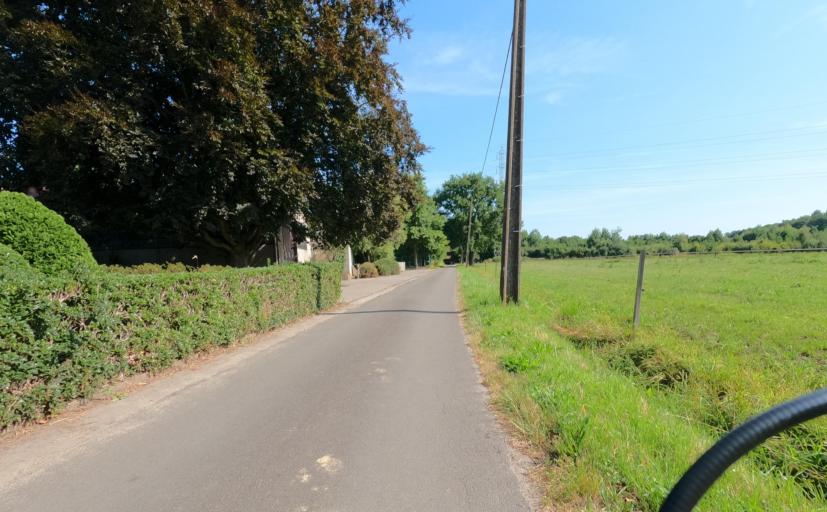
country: BE
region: Flanders
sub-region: Provincie Antwerpen
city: Sint-Katelijne-Waver
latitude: 51.0689
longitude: 4.5541
